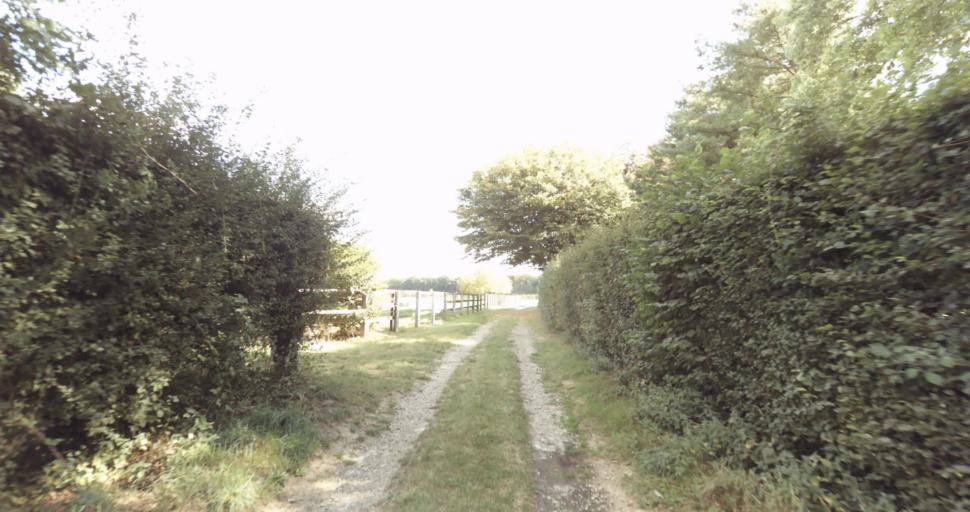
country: FR
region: Lower Normandy
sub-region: Departement de l'Orne
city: Vimoutiers
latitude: 48.9228
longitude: 0.2393
